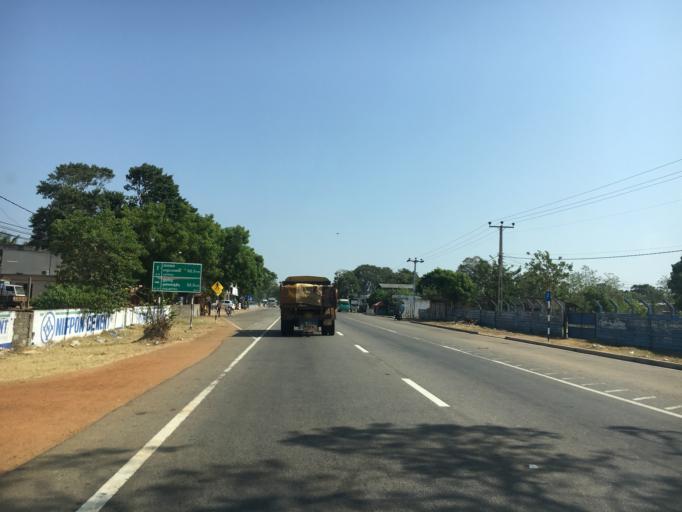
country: LK
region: Northern Province
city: Kilinochchi
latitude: 9.4348
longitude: 80.4077
